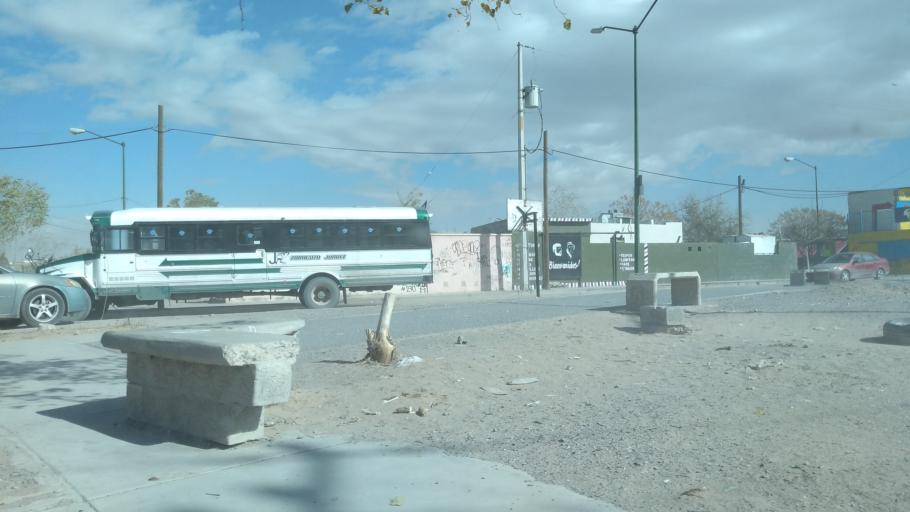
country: US
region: Texas
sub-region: El Paso County
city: Socorro Mission Number 1 Colonia
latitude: 31.5875
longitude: -106.3568
